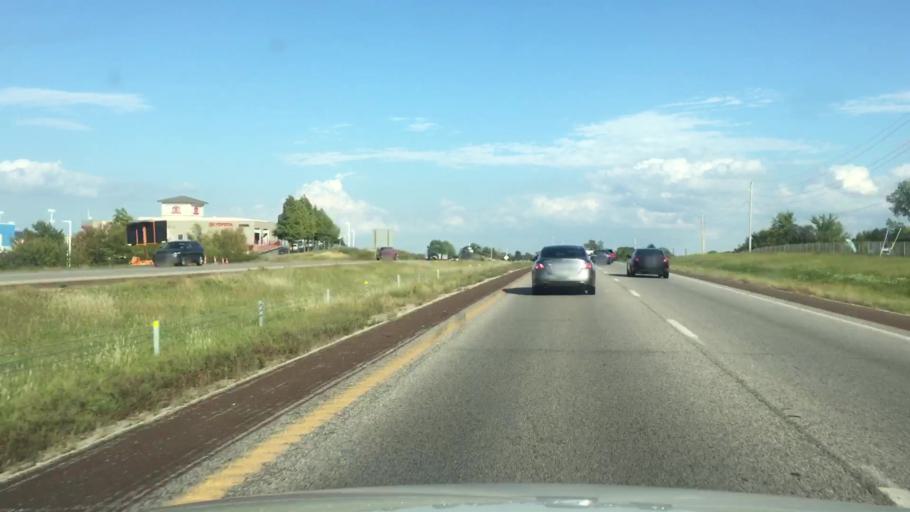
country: US
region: Missouri
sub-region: Jackson County
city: Lees Summit
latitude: 38.9448
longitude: -94.3708
